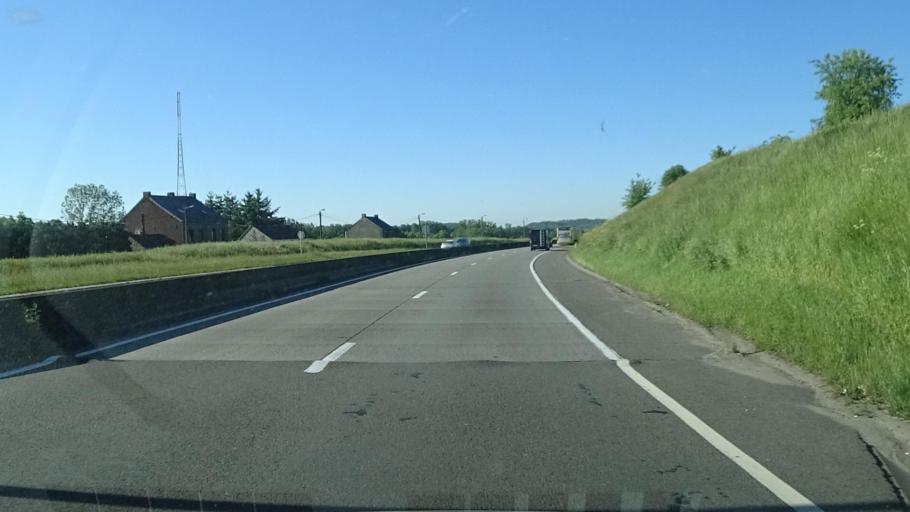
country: BE
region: Wallonia
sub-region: Province du Hainaut
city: Roeulx
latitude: 50.4910
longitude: 4.1360
